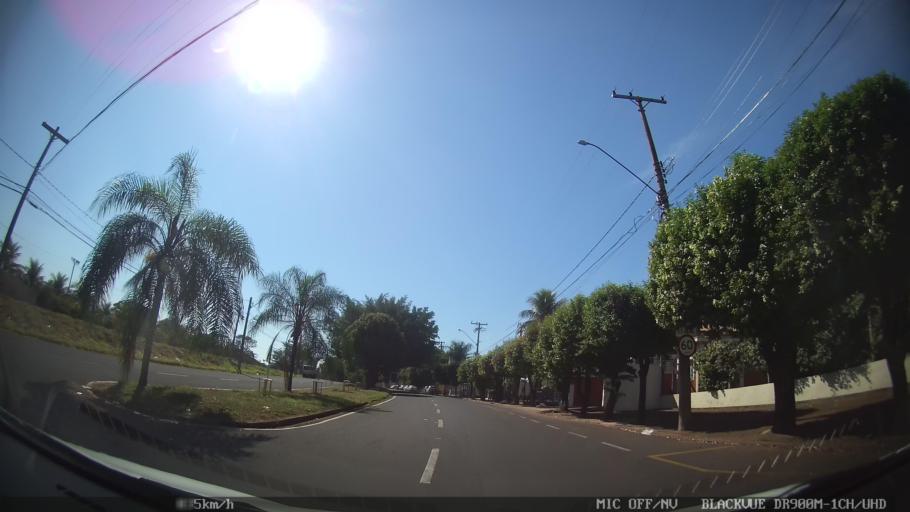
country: BR
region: Sao Paulo
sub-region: Sao Jose Do Rio Preto
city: Sao Jose do Rio Preto
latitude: -20.8143
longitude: -49.4311
